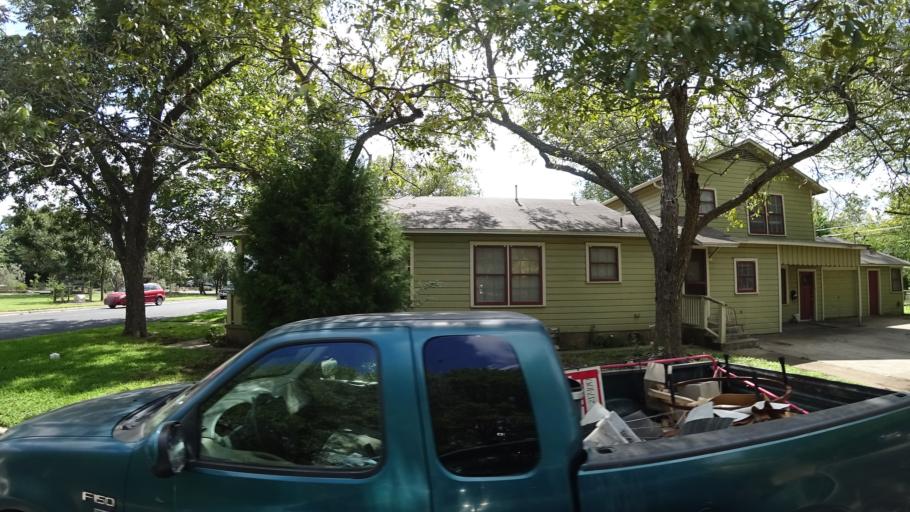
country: US
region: Texas
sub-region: Travis County
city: Austin
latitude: 30.3150
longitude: -97.7185
